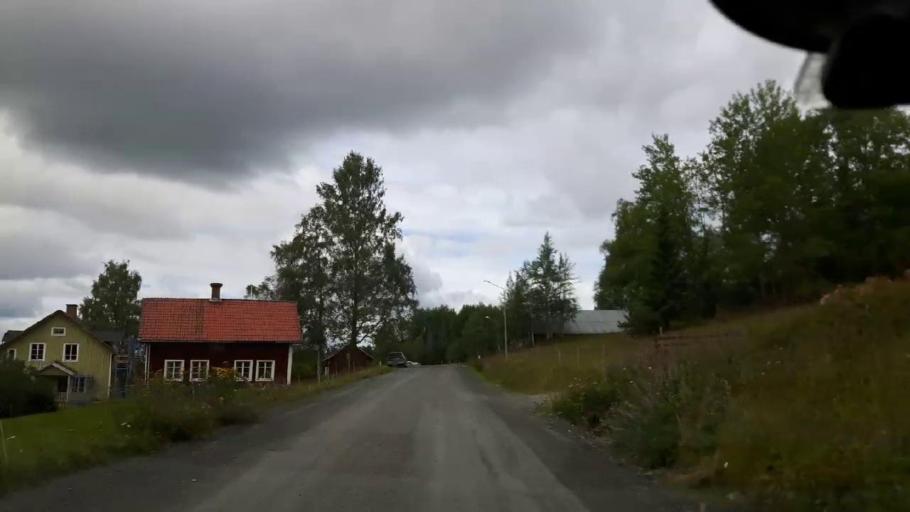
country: SE
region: Jaemtland
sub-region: Krokoms Kommun
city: Valla
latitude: 63.4917
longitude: 13.9832
